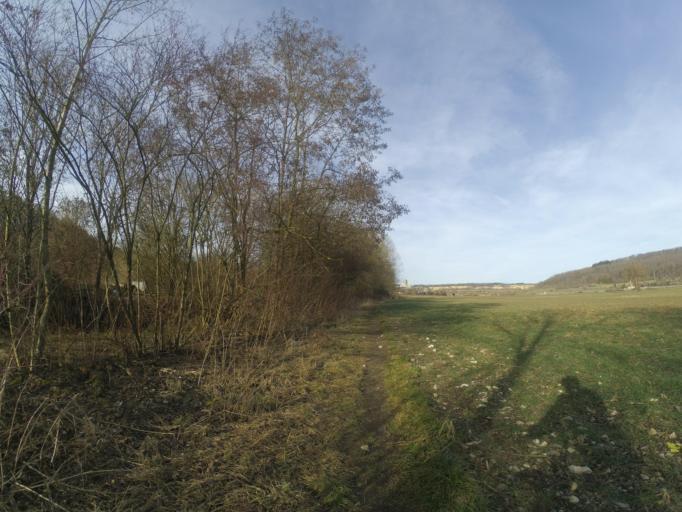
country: DE
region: Baden-Wuerttemberg
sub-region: Regierungsbezirk Stuttgart
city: Bolheim
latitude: 48.6408
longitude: 10.1570
